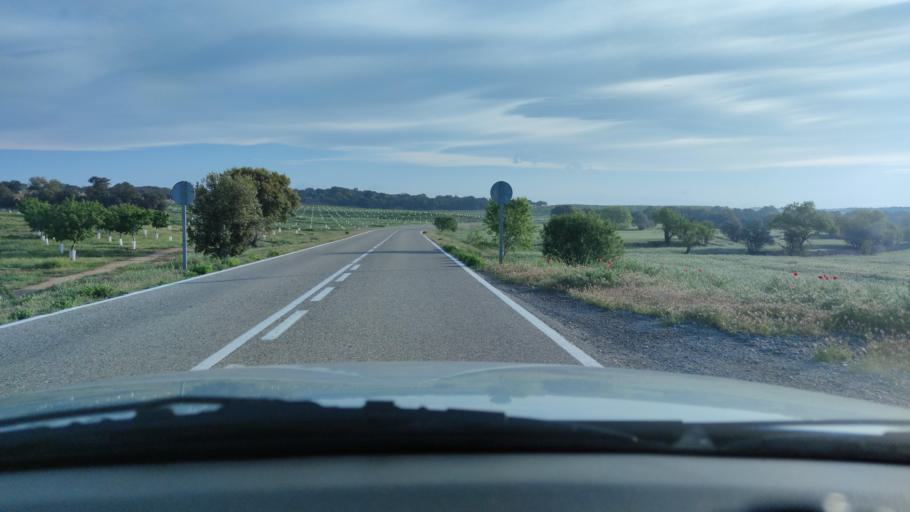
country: ES
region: Catalonia
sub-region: Provincia de Lleida
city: Agramunt
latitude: 41.8201
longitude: 1.0542
